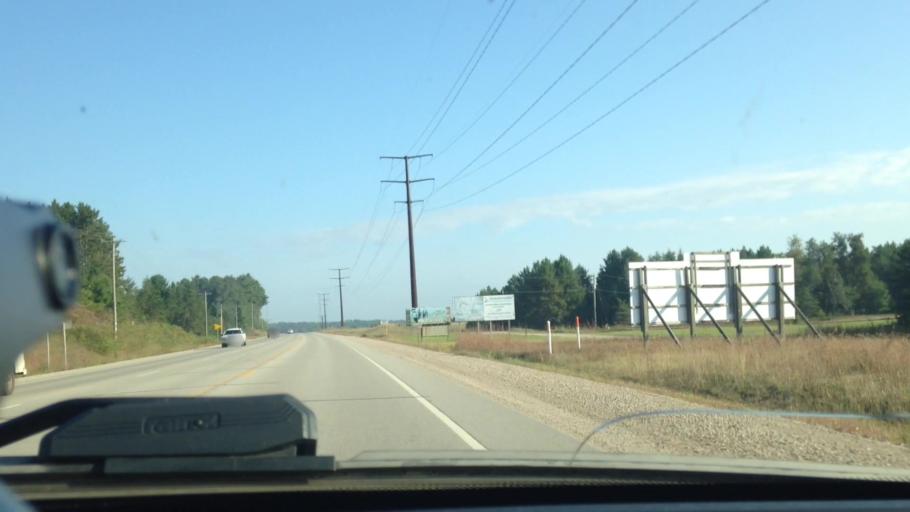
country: US
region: Wisconsin
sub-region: Marinette County
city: Peshtigo
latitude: 45.1971
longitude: -87.9944
